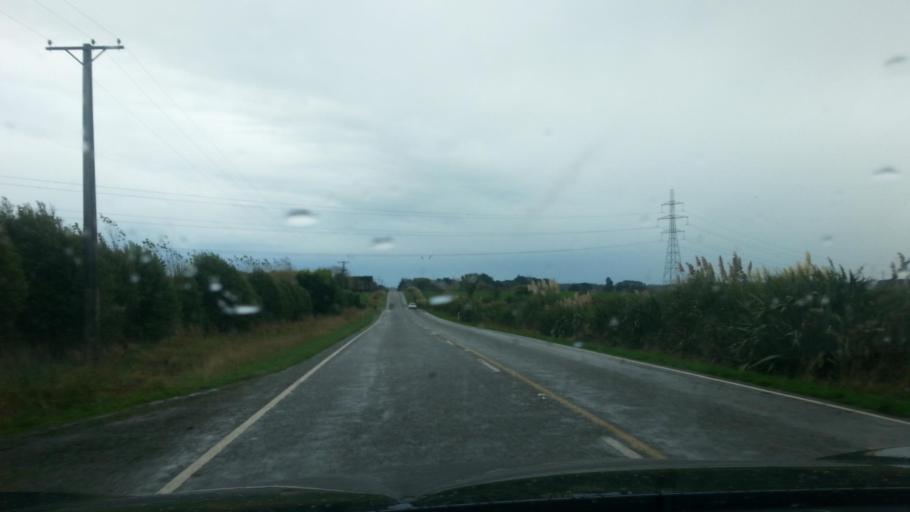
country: NZ
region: Southland
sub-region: Invercargill City
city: Invercargill
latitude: -46.3471
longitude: 168.4133
